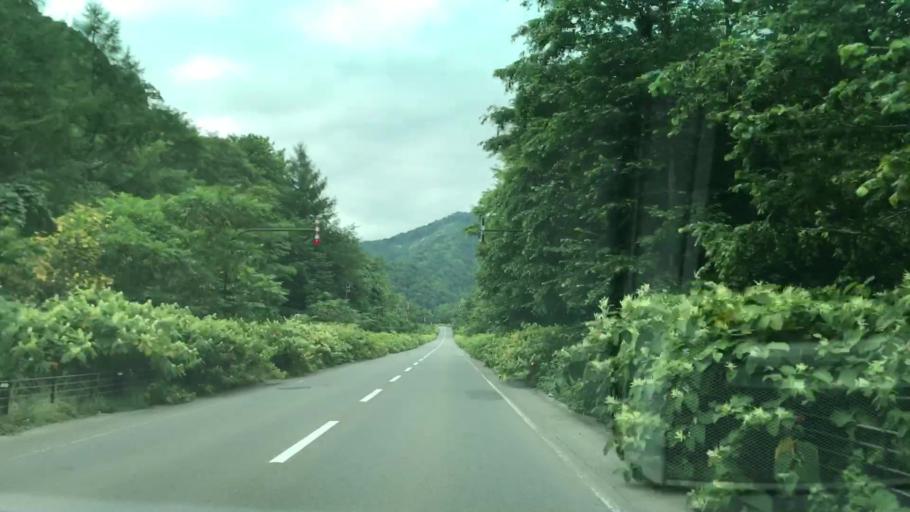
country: JP
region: Hokkaido
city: Yoichi
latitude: 43.0203
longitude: 140.8678
